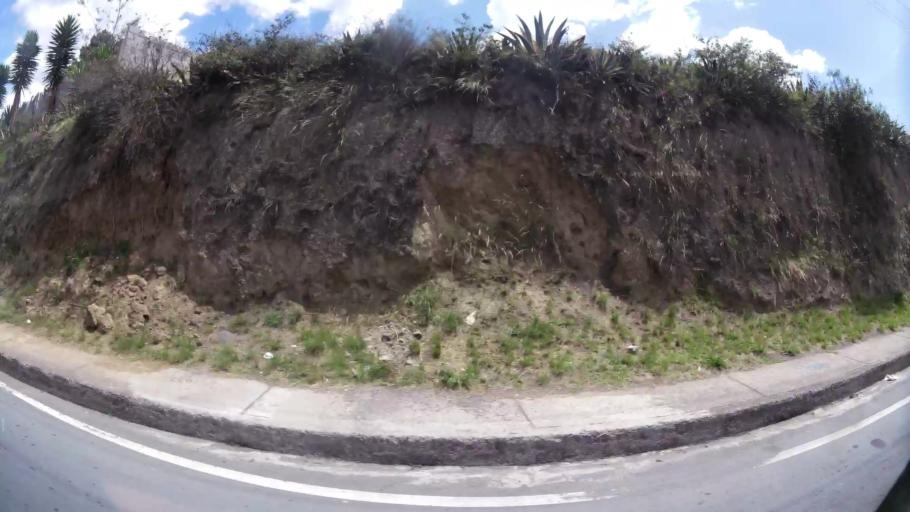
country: EC
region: Pichincha
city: Quito
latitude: -0.1017
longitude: -78.4194
